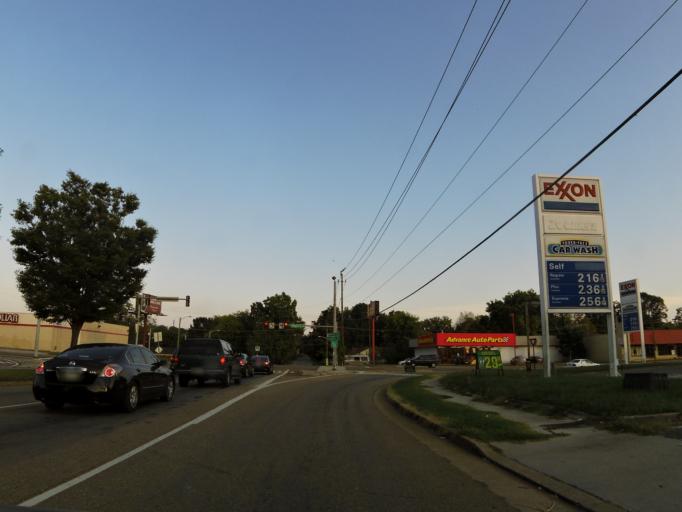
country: US
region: Tennessee
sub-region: Knox County
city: Knoxville
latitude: 35.9873
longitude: -83.8944
